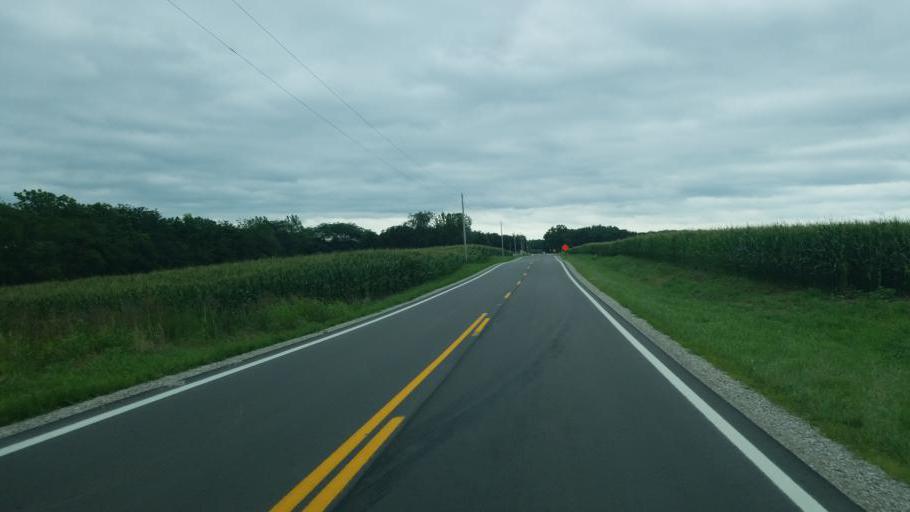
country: US
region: Ohio
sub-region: Pickaway County
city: South Bloomfield
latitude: 39.6834
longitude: -83.0030
